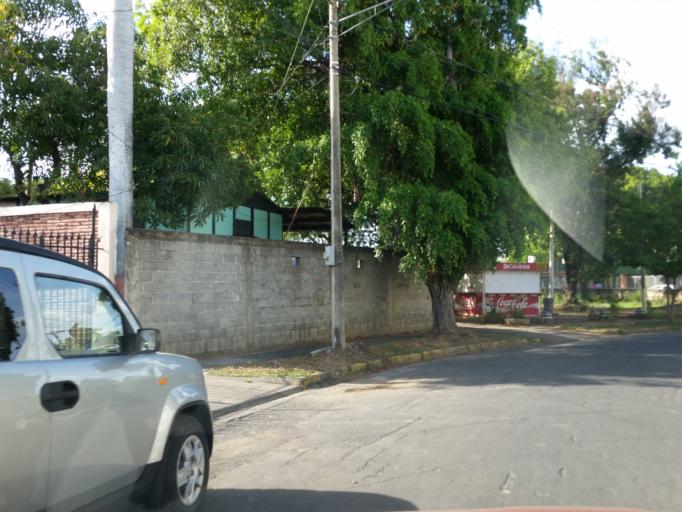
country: NI
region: Managua
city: Managua
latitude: 12.1360
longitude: -86.2673
